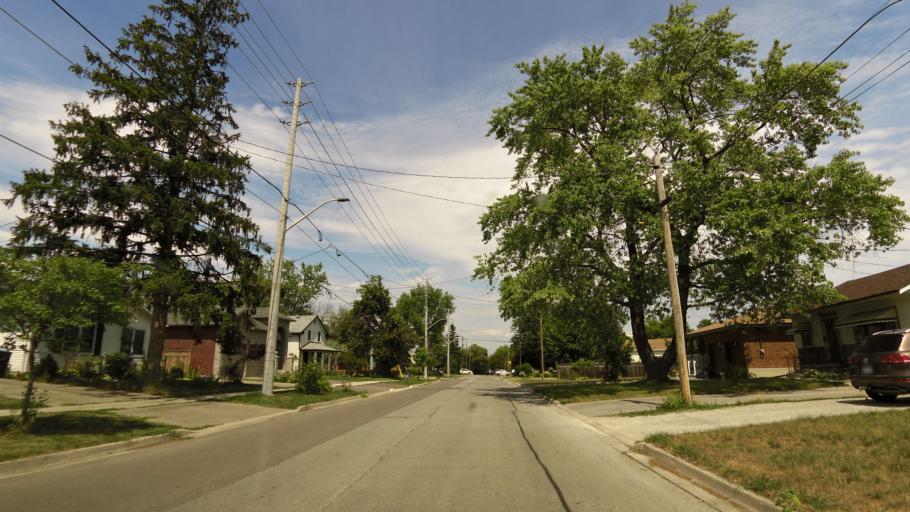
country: CA
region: Ontario
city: Mississauga
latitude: 43.5668
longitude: -79.5764
